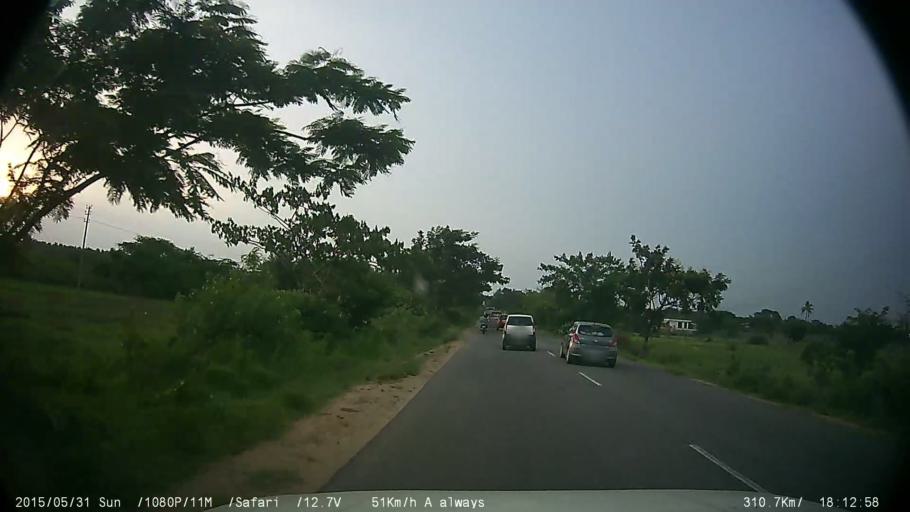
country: IN
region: Karnataka
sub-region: Mysore
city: Nanjangud
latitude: 12.0994
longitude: 76.6719
